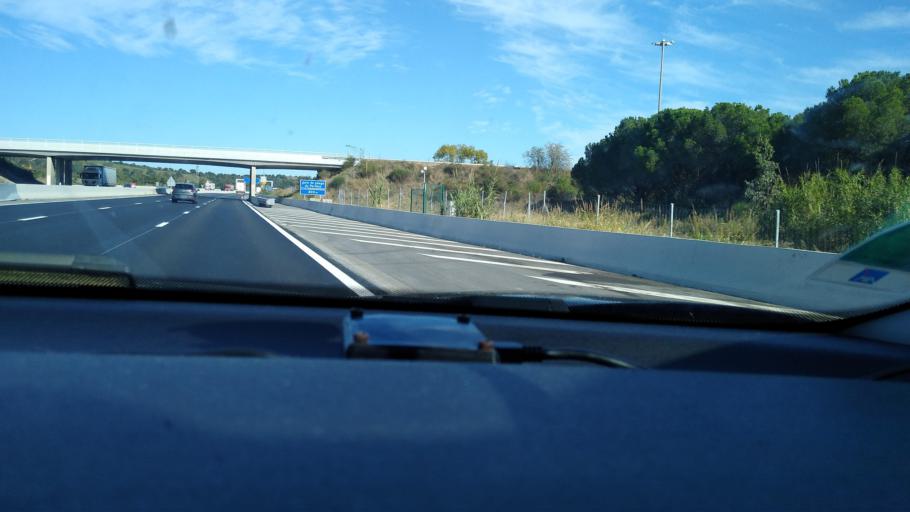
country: FR
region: Languedoc-Roussillon
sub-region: Departement des Pyrenees-Orientales
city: el Volo
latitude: 42.5199
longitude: 2.8191
